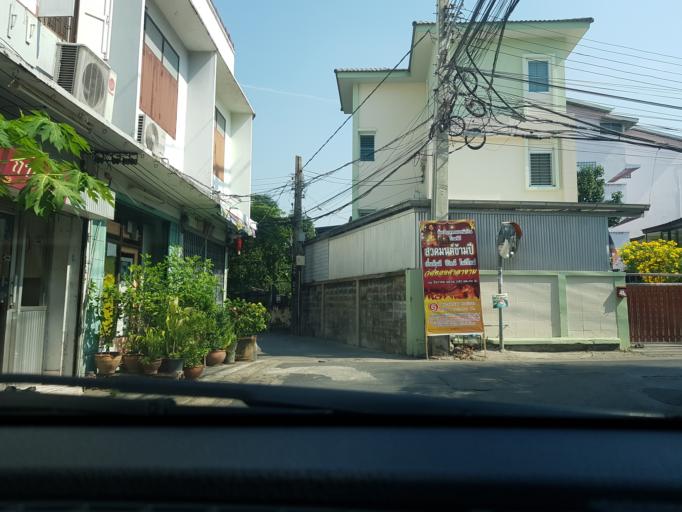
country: TH
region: Bangkok
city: Bangkok Yai
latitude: 13.7258
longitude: 100.4654
